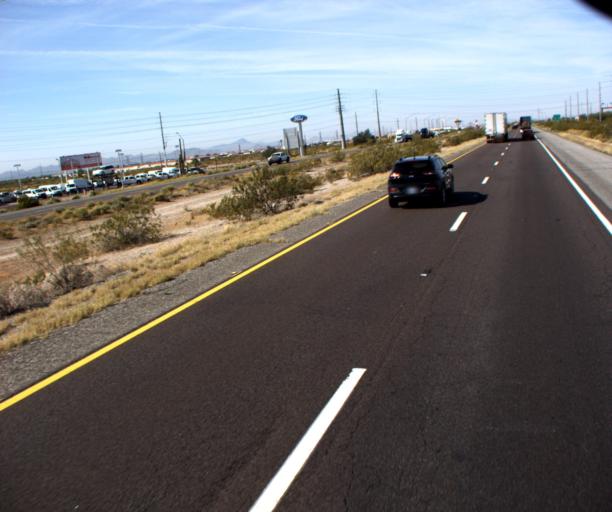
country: US
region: Arizona
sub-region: Maricopa County
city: Buckeye
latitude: 33.4369
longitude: -112.5812
